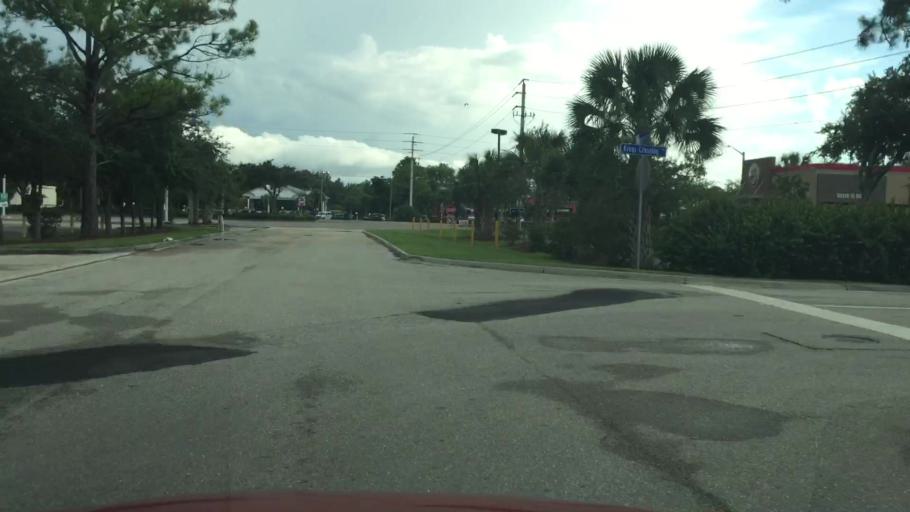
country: US
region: Florida
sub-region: Lee County
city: Gateway
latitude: 26.5483
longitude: -81.8021
